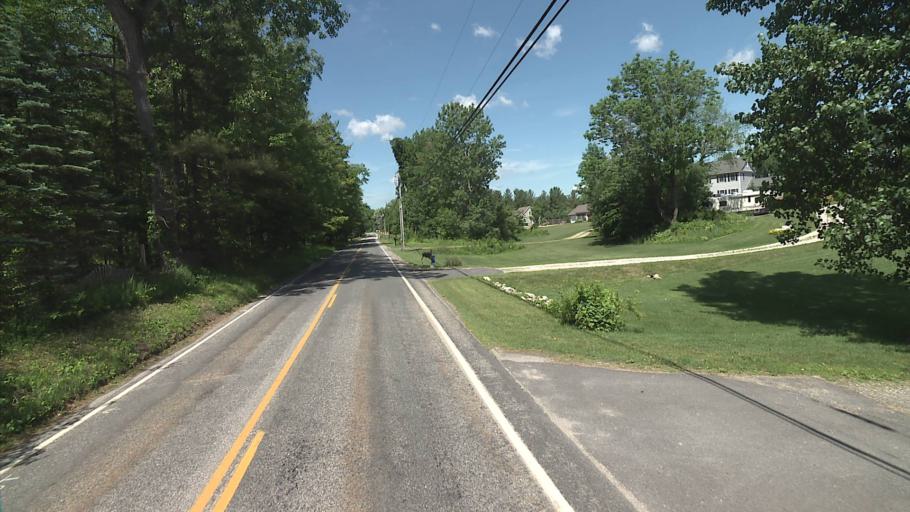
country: US
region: Connecticut
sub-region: Litchfield County
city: Canaan
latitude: 42.0465
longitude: -73.3131
